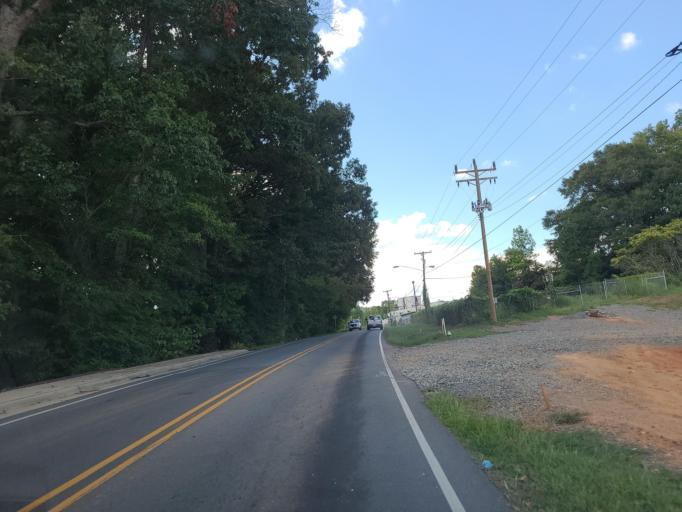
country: US
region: North Carolina
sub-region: Gaston County
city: Lowell
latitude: 35.2835
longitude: -81.1046
